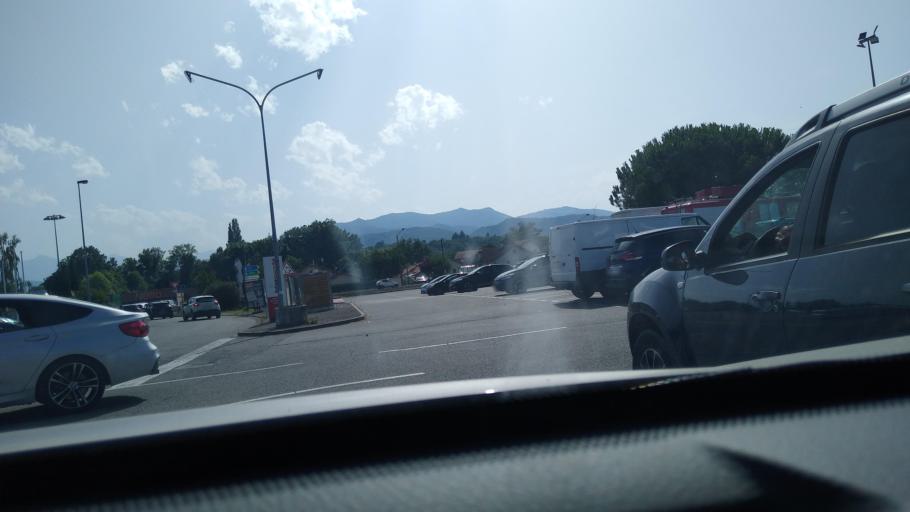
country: FR
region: Midi-Pyrenees
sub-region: Departement de l'Ariege
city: Saint-Lizier
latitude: 43.0058
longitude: 1.1276
